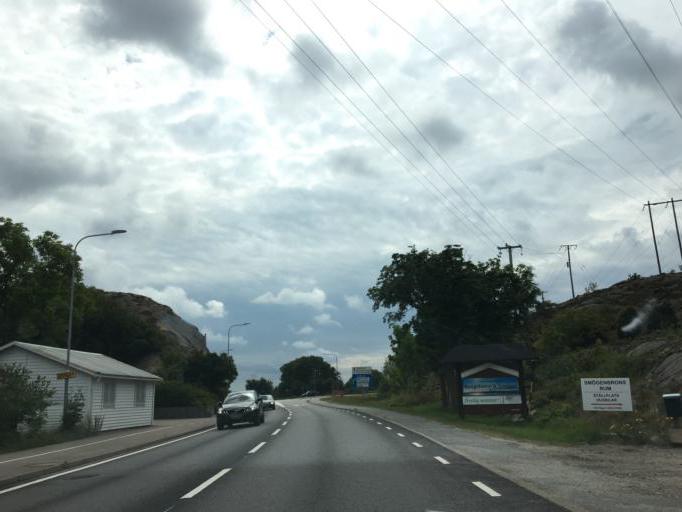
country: SE
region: Vaestra Goetaland
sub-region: Sotenas Kommun
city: Kungshamn
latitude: 58.3692
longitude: 11.2500
